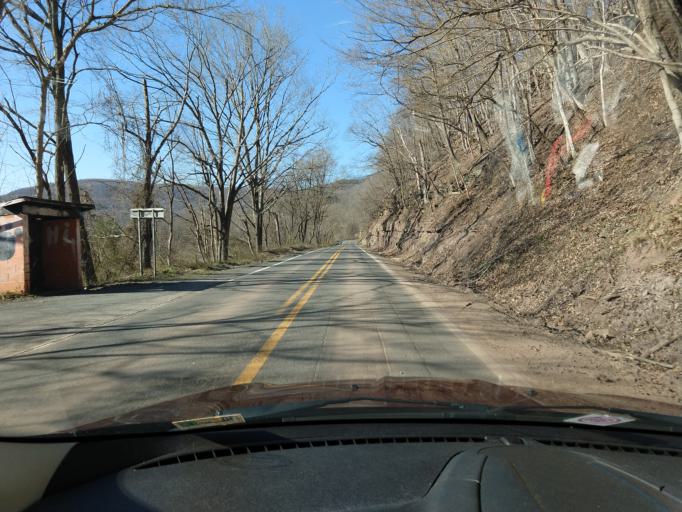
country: US
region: West Virginia
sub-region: Summers County
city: Hinton
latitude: 37.7197
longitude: -80.8877
